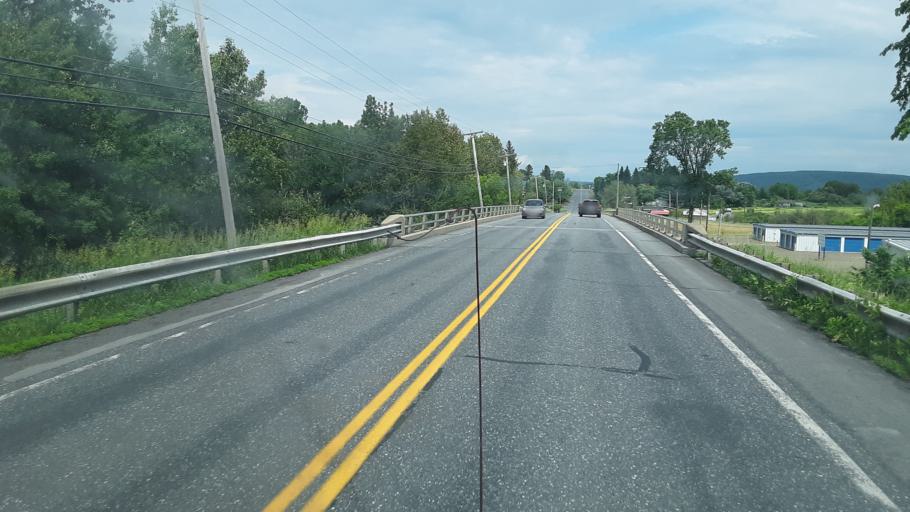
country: US
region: Maine
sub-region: Aroostook County
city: Fort Fairfield
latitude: 46.7628
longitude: -67.8537
